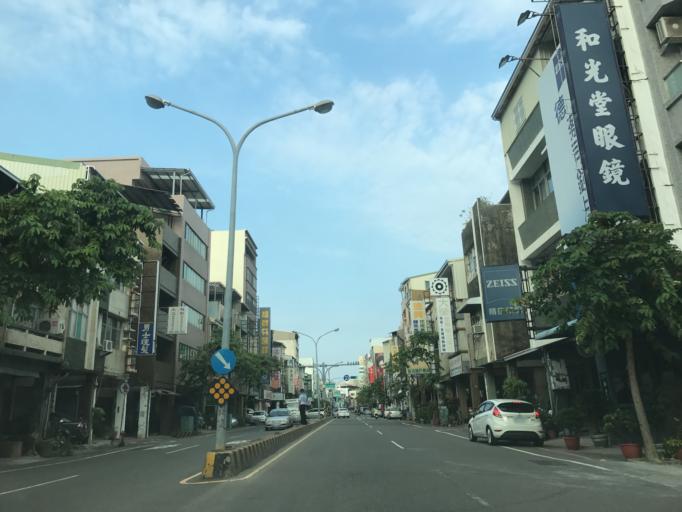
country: TW
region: Taiwan
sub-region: Tainan
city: Tainan
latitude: 22.9995
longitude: 120.1912
